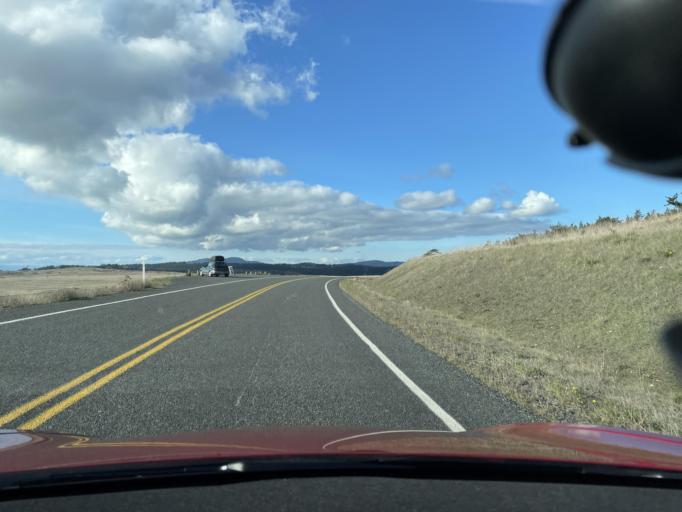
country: US
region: Washington
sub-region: San Juan County
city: Friday Harbor
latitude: 48.4571
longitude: -122.9921
